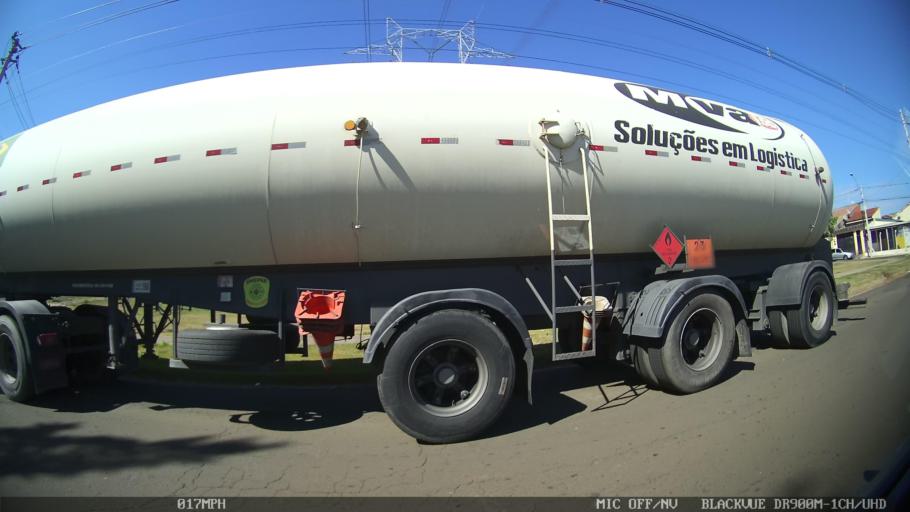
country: BR
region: Sao Paulo
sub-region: Santa Barbara D'Oeste
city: Santa Barbara d'Oeste
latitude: -22.7338
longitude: -47.4088
